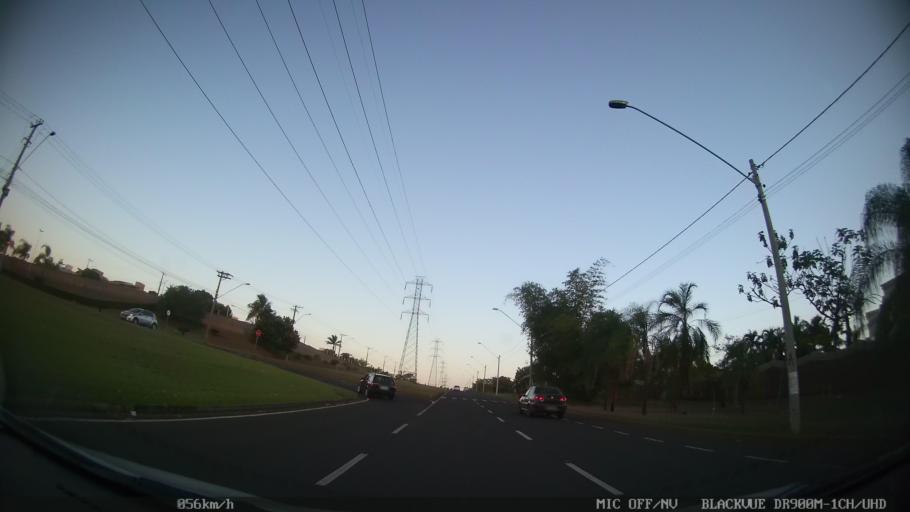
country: BR
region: Sao Paulo
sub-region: Sao Jose Do Rio Preto
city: Sao Jose do Rio Preto
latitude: -20.8135
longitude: -49.3399
